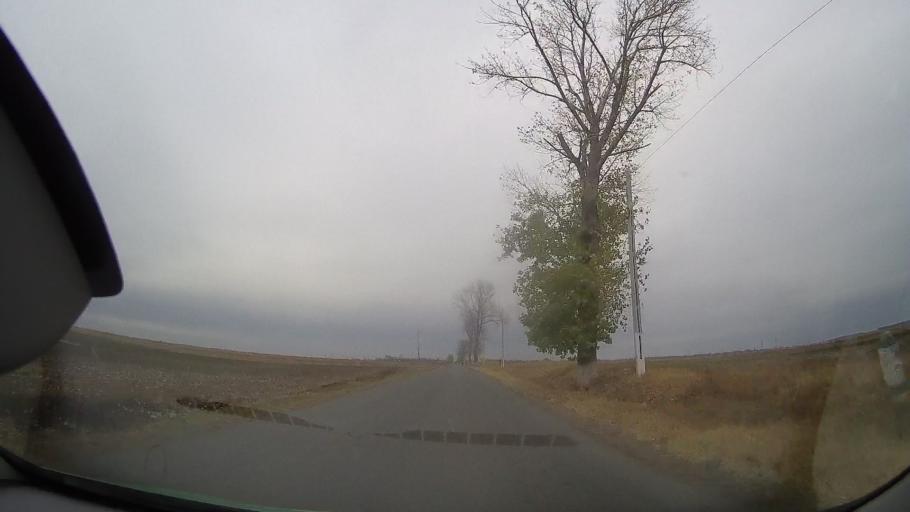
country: RO
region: Braila
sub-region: Comuna Budesti
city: Tataru
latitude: 44.8681
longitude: 27.4277
